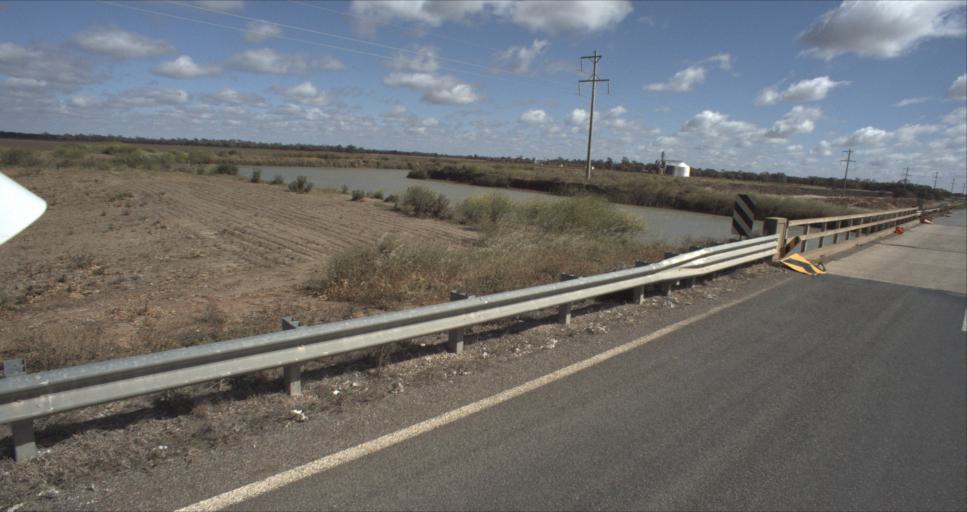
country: AU
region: New South Wales
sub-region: Murrumbidgee Shire
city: Darlington Point
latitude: -34.5532
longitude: 146.1703
